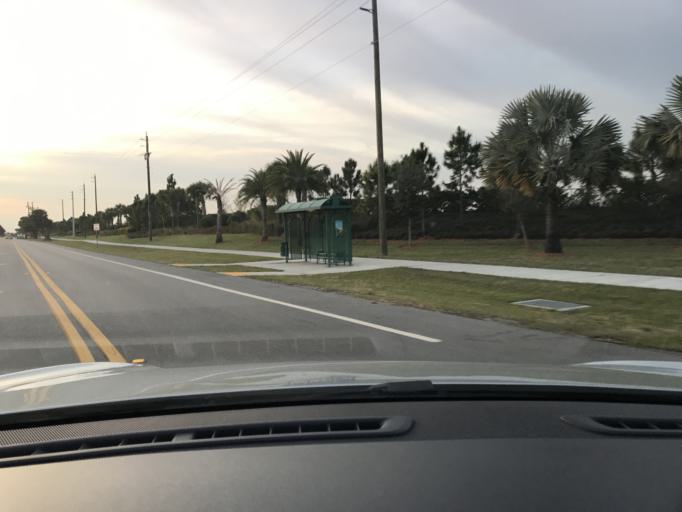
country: US
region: Florida
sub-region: Indian River County
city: Gifford
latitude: 27.6825
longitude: -80.4297
